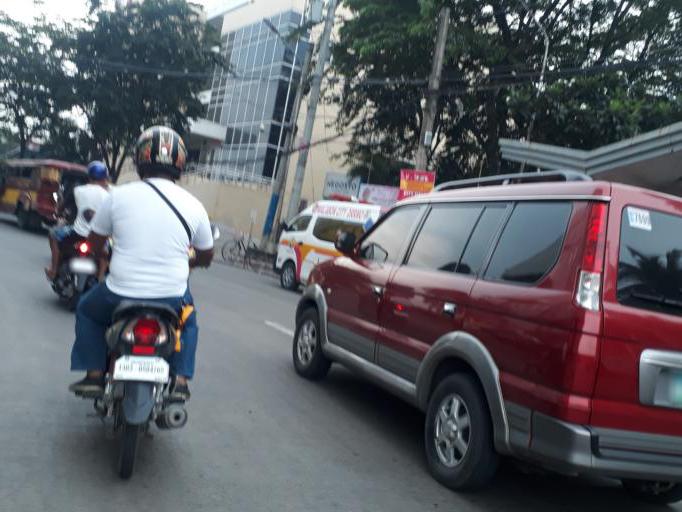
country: PH
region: Metro Manila
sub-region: Caloocan City
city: Niugan
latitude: 14.6578
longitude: 120.9508
